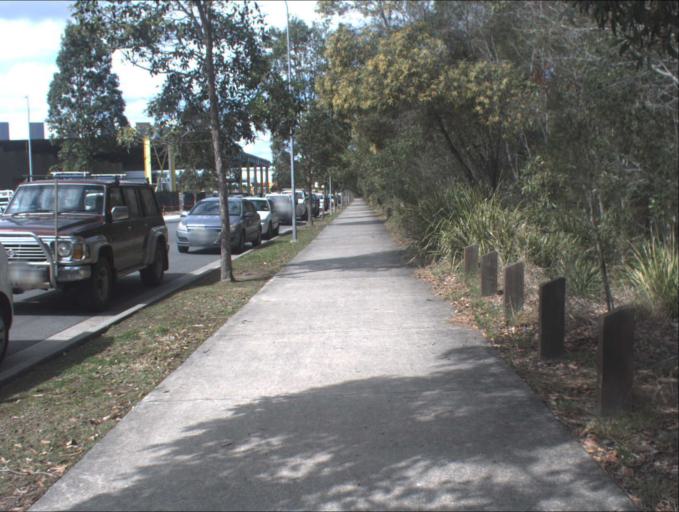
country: AU
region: Queensland
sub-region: Logan
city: Woodridge
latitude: -27.6671
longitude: 153.0758
